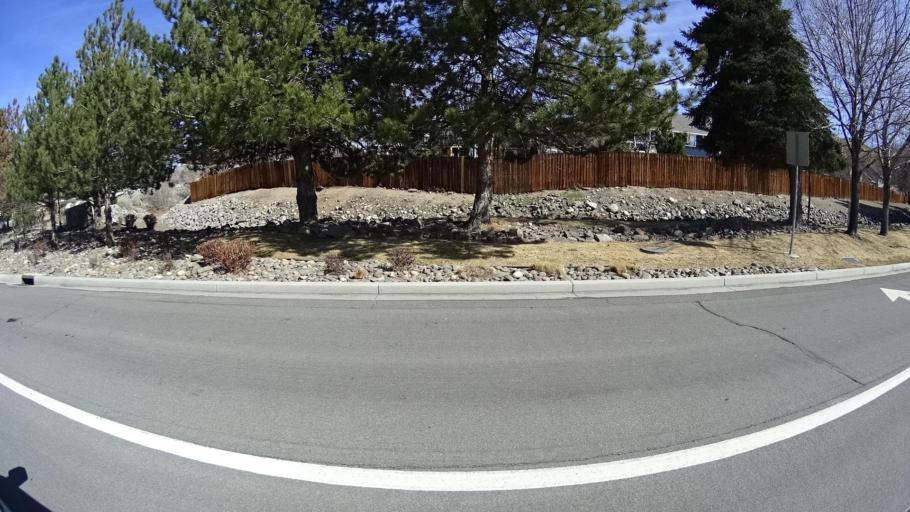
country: US
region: Nevada
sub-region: Washoe County
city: Sun Valley
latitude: 39.5859
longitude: -119.7142
